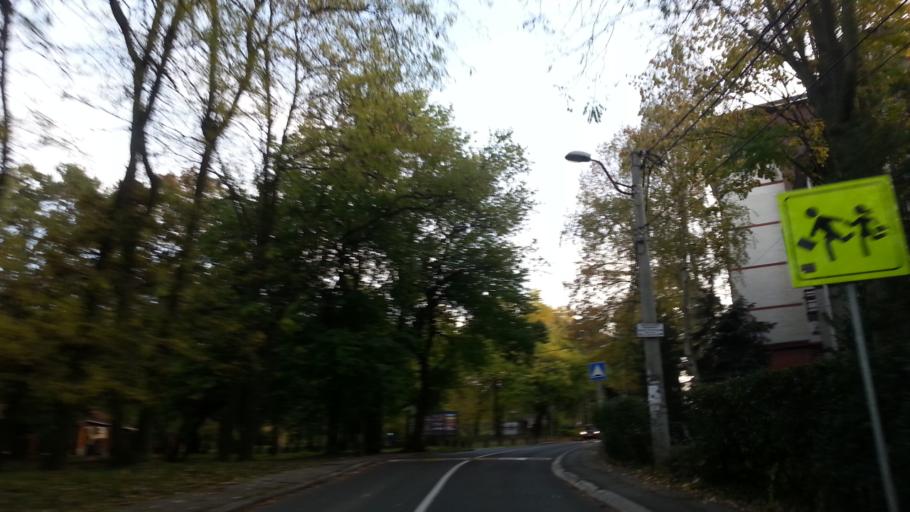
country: RS
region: Central Serbia
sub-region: Belgrade
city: Cukarica
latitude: 44.7771
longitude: 20.4240
